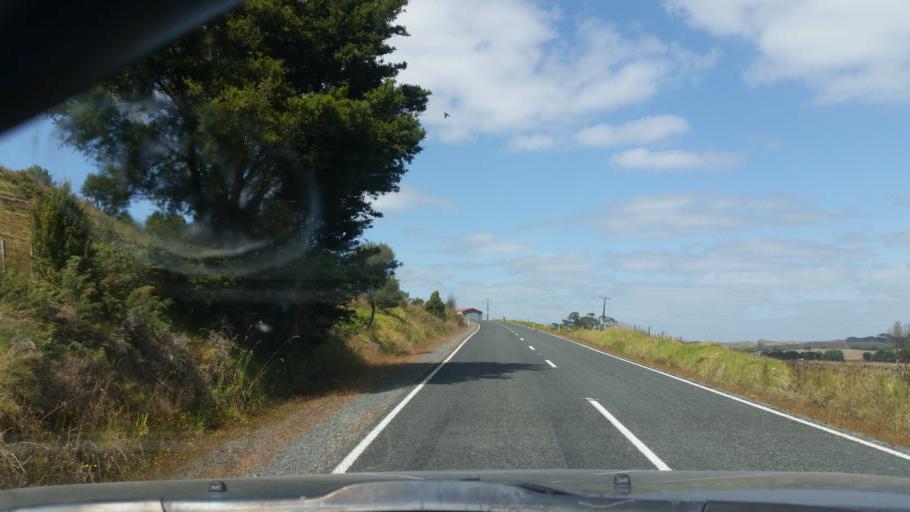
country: NZ
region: Northland
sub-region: Whangarei
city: Ruakaka
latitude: -35.9506
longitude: 174.2935
